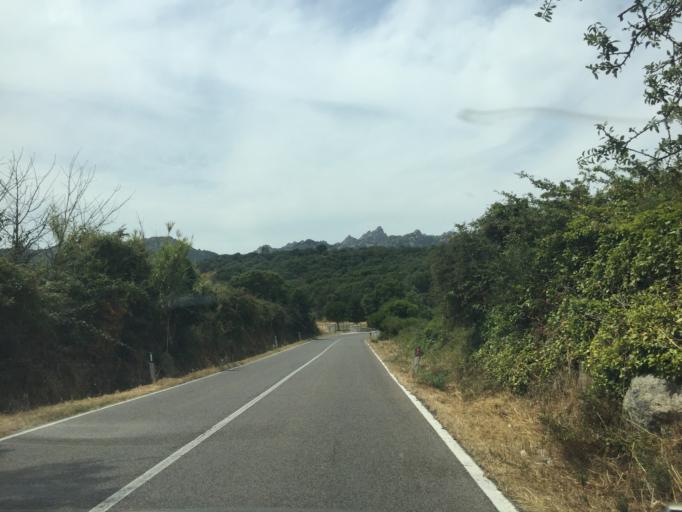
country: IT
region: Sardinia
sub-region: Provincia di Olbia-Tempio
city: Aggius
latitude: 40.9150
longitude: 9.0737
